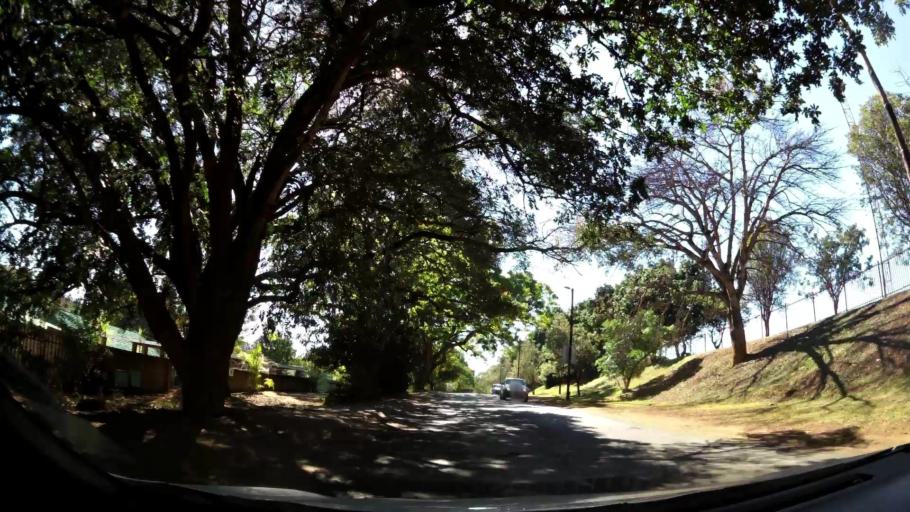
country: ZA
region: Limpopo
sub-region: Mopani District Municipality
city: Tzaneen
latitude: -23.8306
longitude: 30.1530
